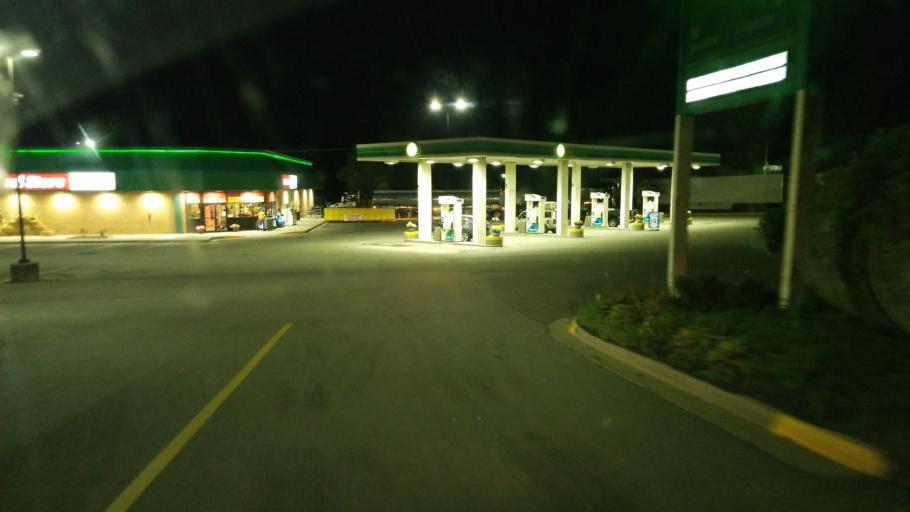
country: US
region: Ohio
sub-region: Preble County
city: New Paris
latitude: 39.8340
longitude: -84.8107
